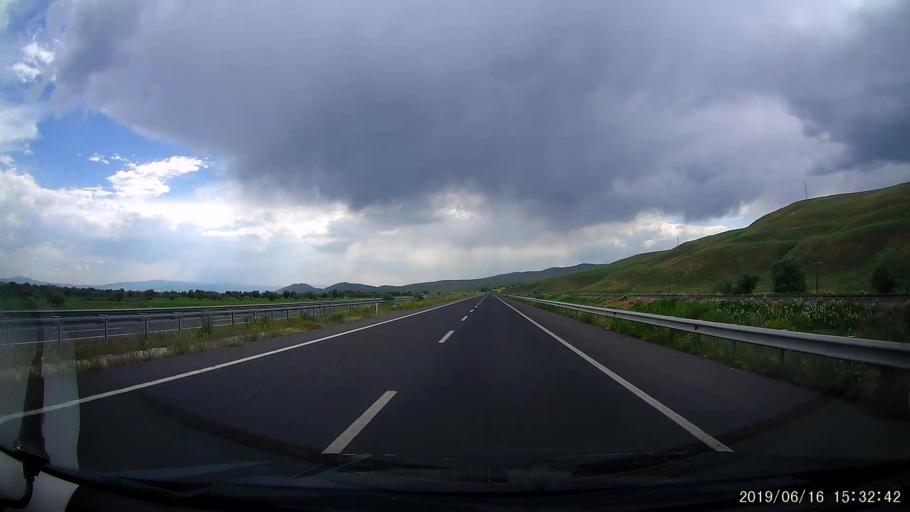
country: TR
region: Erzurum
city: Horasan
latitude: 40.0297
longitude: 42.0399
